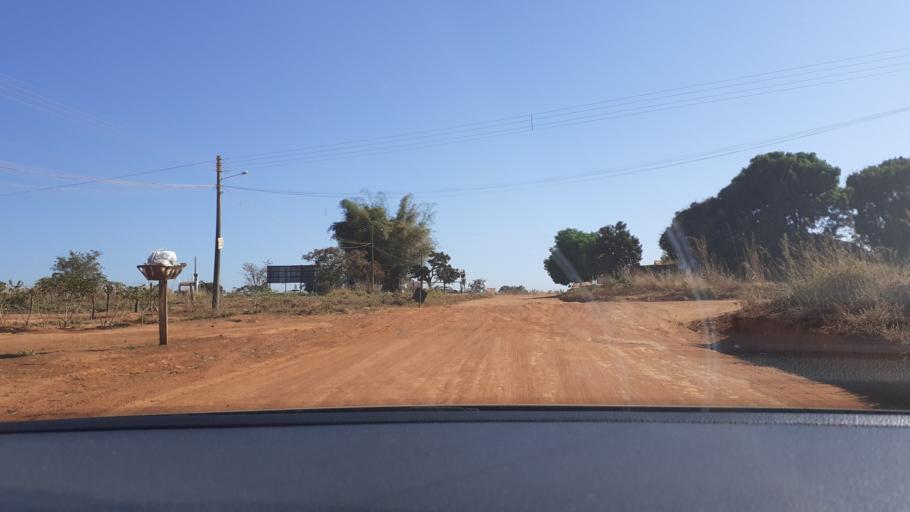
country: BR
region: Goias
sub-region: Aparecida De Goiania
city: Aparecida de Goiania
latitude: -16.8664
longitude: -49.2559
